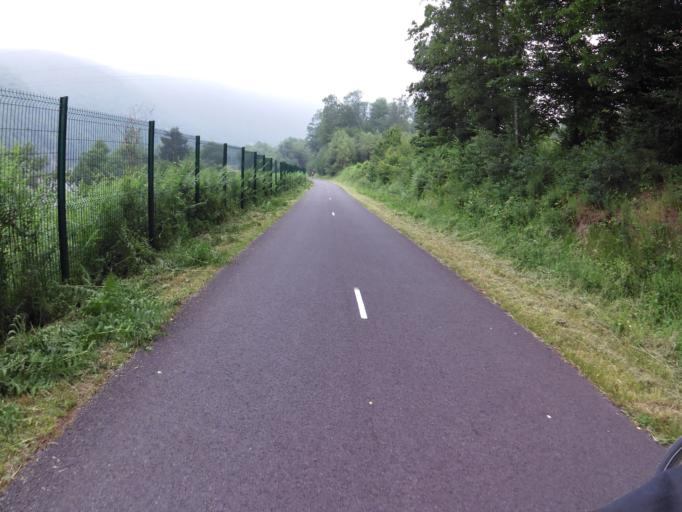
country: FR
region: Champagne-Ardenne
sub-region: Departement des Ardennes
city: Revin
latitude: 49.9689
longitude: 4.6647
